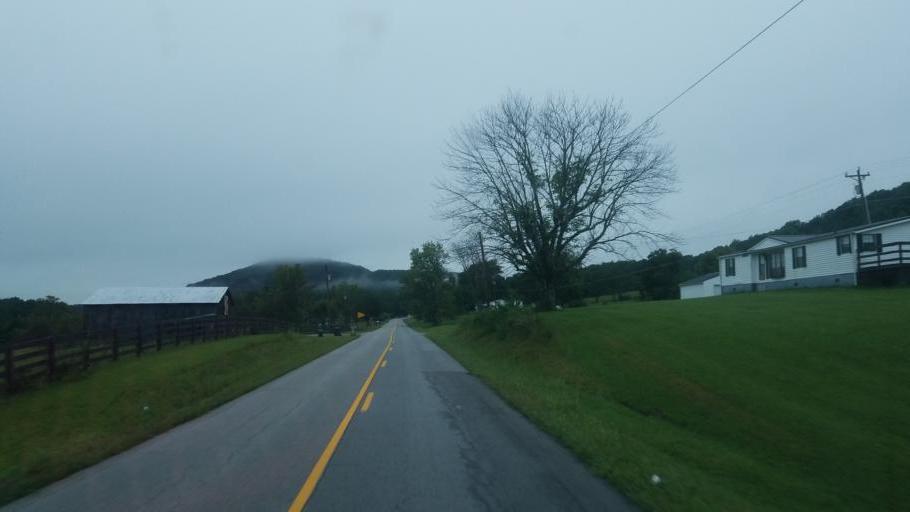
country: US
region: Kentucky
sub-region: Fleming County
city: Flemingsburg
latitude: 38.4042
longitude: -83.6345
